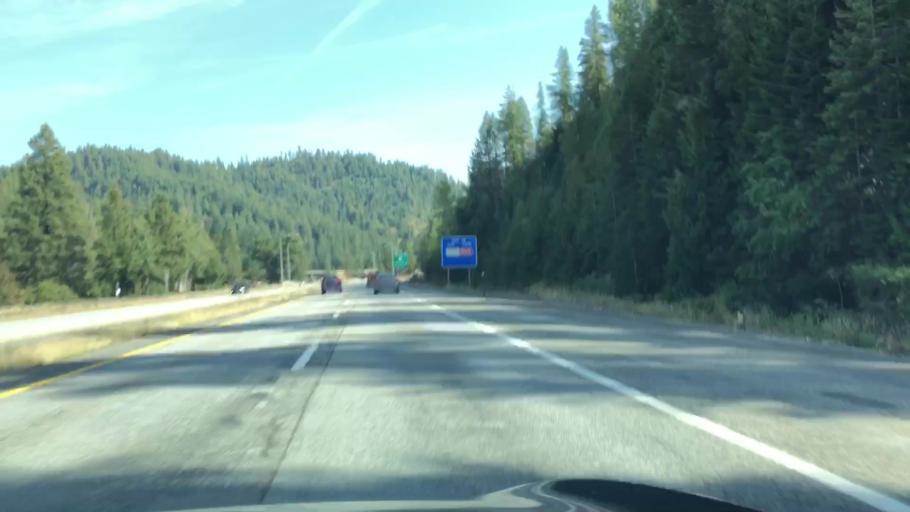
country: US
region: Idaho
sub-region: Shoshone County
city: Pinehurst
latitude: 47.5766
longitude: -116.4502
